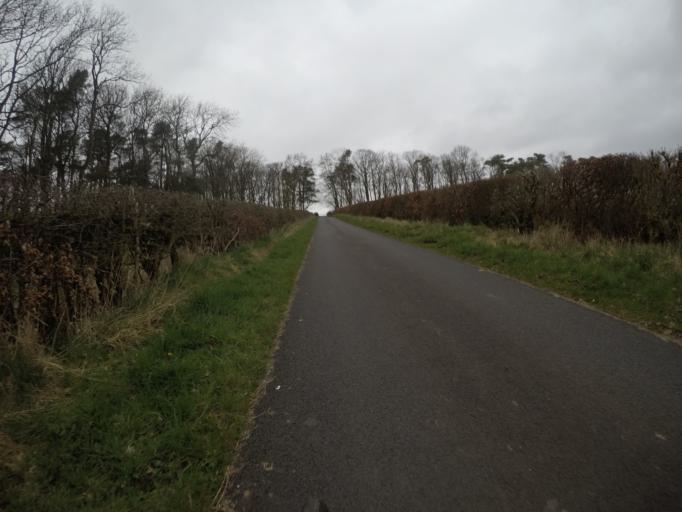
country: GB
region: Scotland
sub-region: East Ayrshire
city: Galston
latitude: 55.6232
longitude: -4.3559
